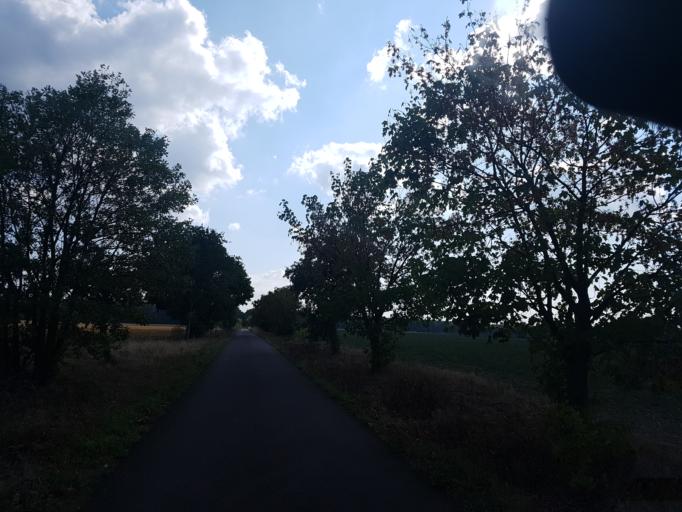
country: DE
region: Brandenburg
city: Gorzke
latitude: 52.0635
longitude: 12.3007
